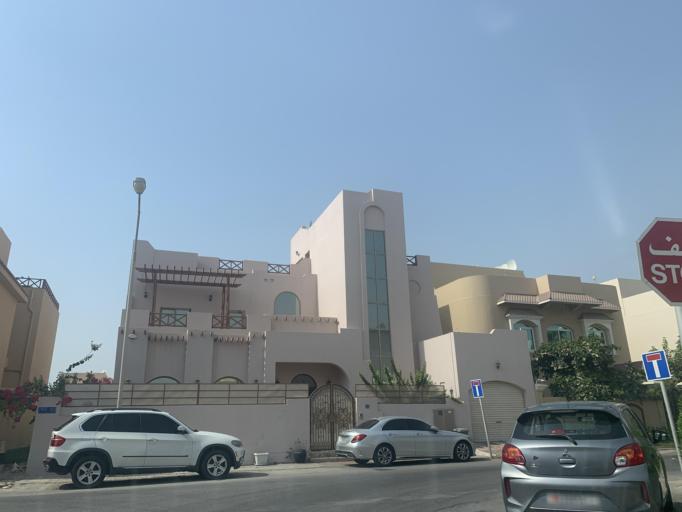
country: BH
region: Manama
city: Jidd Hafs
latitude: 26.2067
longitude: 50.4932
